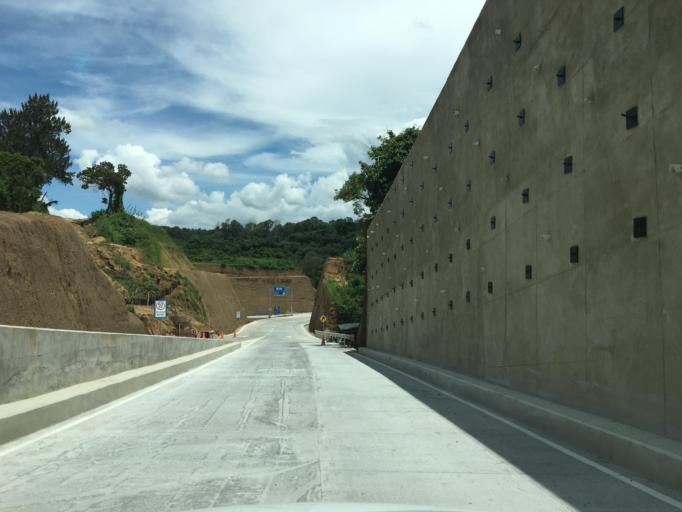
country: GT
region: Guatemala
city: Santa Catarina Pinula
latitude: 14.5746
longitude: -90.5409
